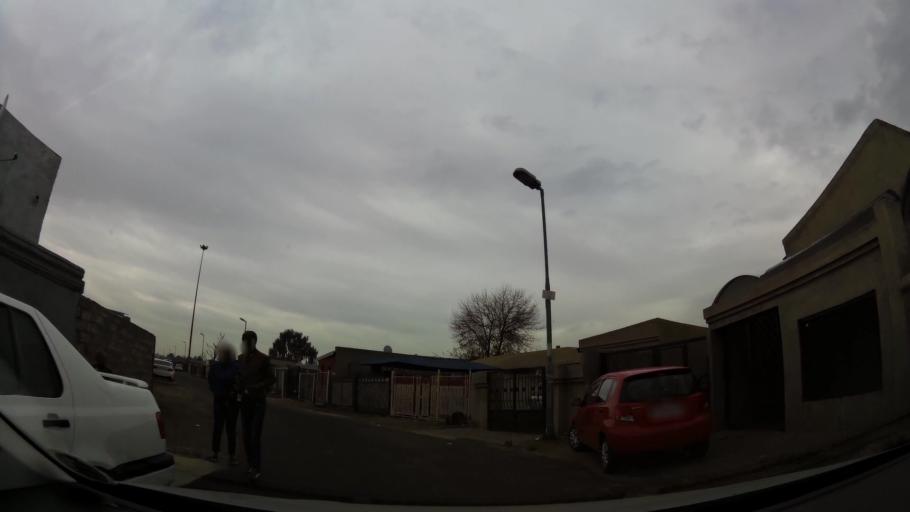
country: ZA
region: Gauteng
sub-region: City of Johannesburg Metropolitan Municipality
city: Soweto
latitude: -26.2562
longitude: 27.8761
